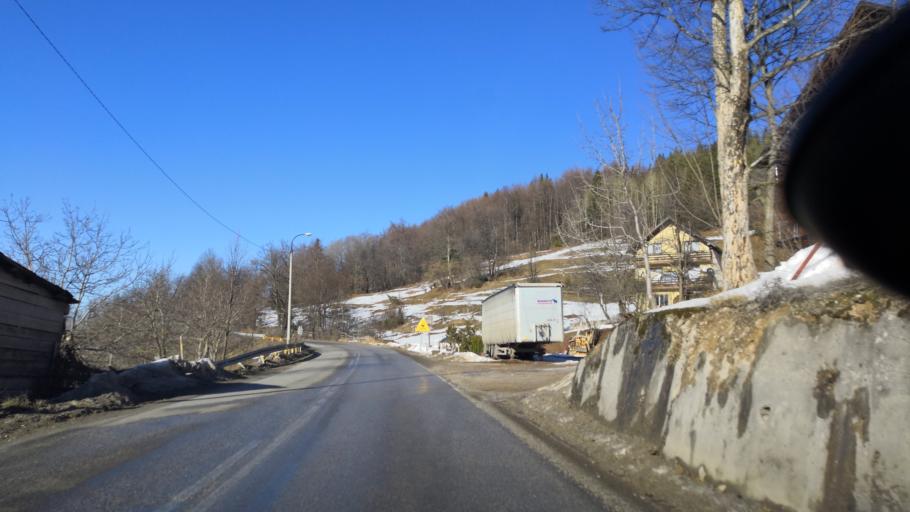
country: BA
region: Republika Srpska
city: Pale
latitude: 43.8957
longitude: 18.6362
